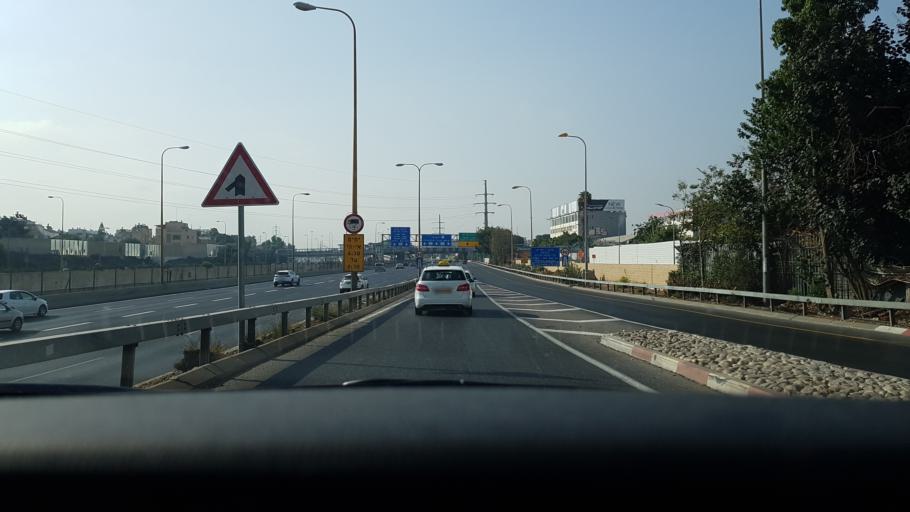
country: IL
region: Tel Aviv
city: Tel Aviv
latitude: 32.0585
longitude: 34.7853
